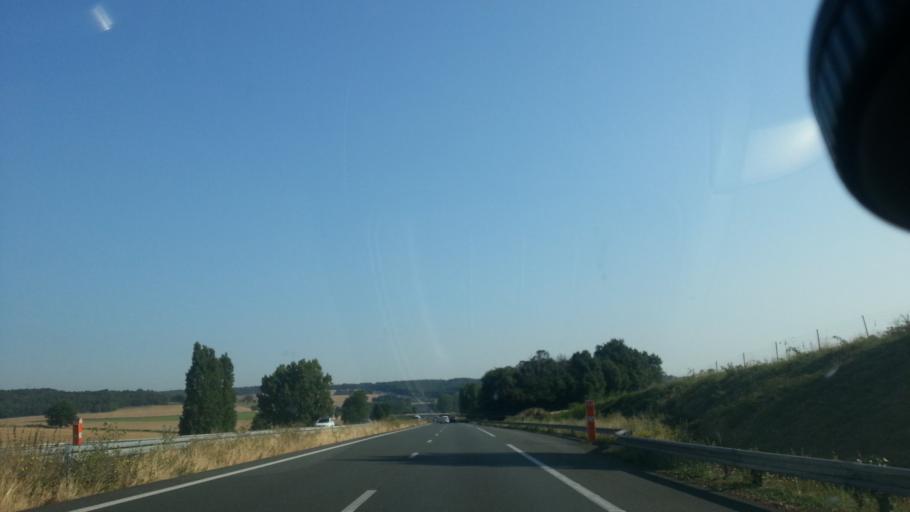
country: FR
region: Poitou-Charentes
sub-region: Departement de la Vienne
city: Dange-Saint-Romain
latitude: 46.9365
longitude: 0.5444
